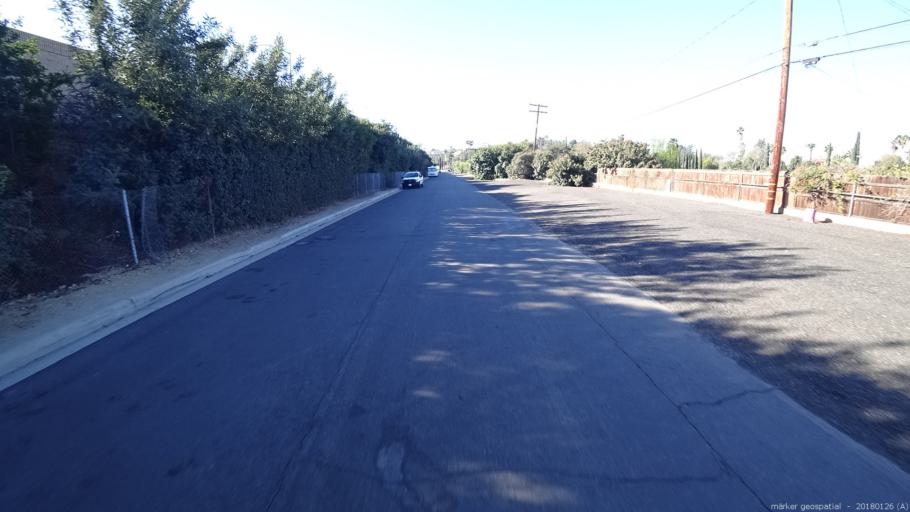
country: US
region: California
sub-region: Los Angeles County
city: Walnut
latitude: 33.9978
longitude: -117.8394
